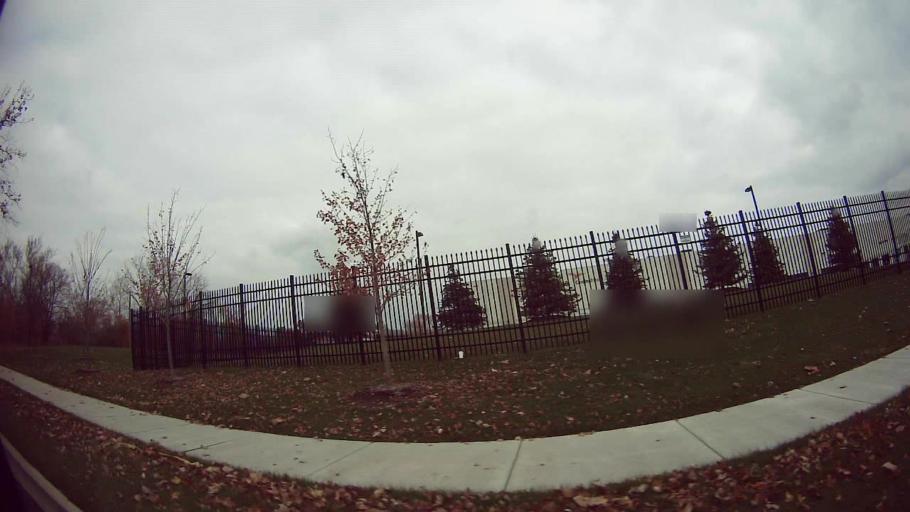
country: US
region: Michigan
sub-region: Wayne County
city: Highland Park
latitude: 42.3594
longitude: -83.0879
